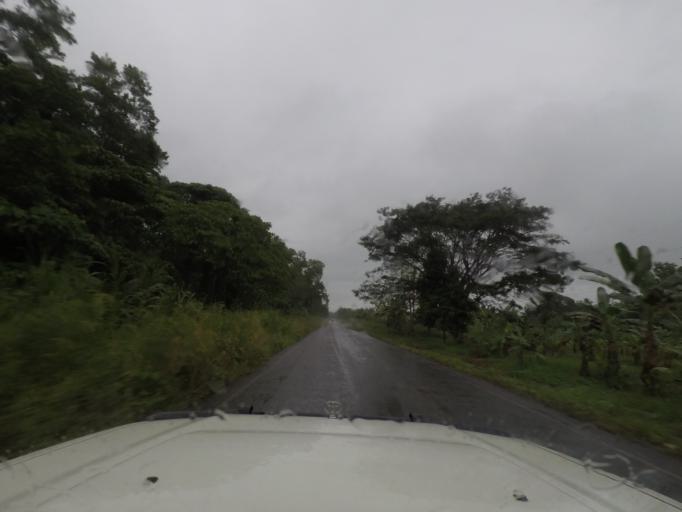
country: PG
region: Madang
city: Madang
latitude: -5.3509
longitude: 145.7101
